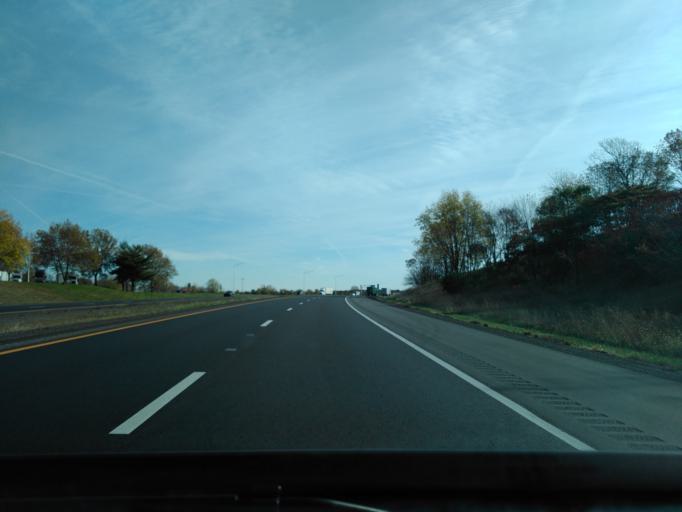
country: US
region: Illinois
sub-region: Madison County
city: Highland
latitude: 38.7873
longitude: -89.6886
